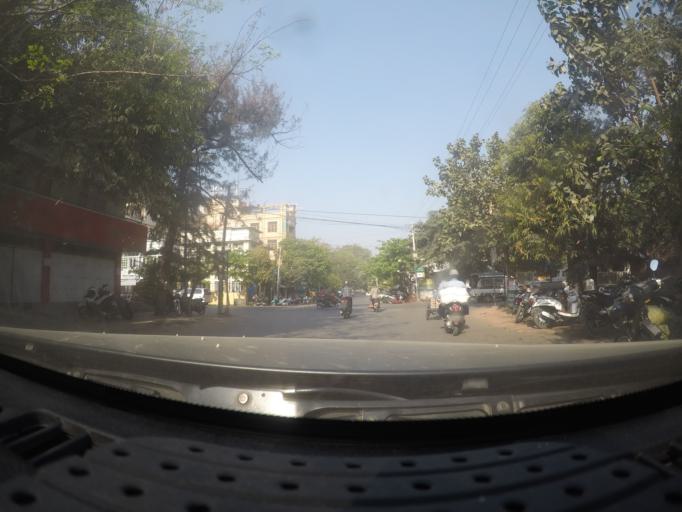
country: MM
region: Mandalay
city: Mandalay
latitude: 21.9665
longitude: 96.0787
